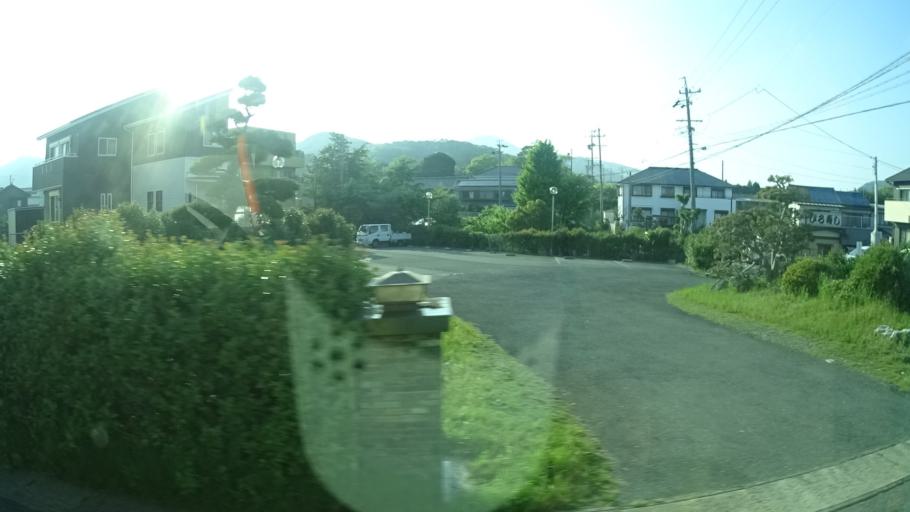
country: JP
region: Aichi
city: Tahara
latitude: 34.6644
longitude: 137.2585
